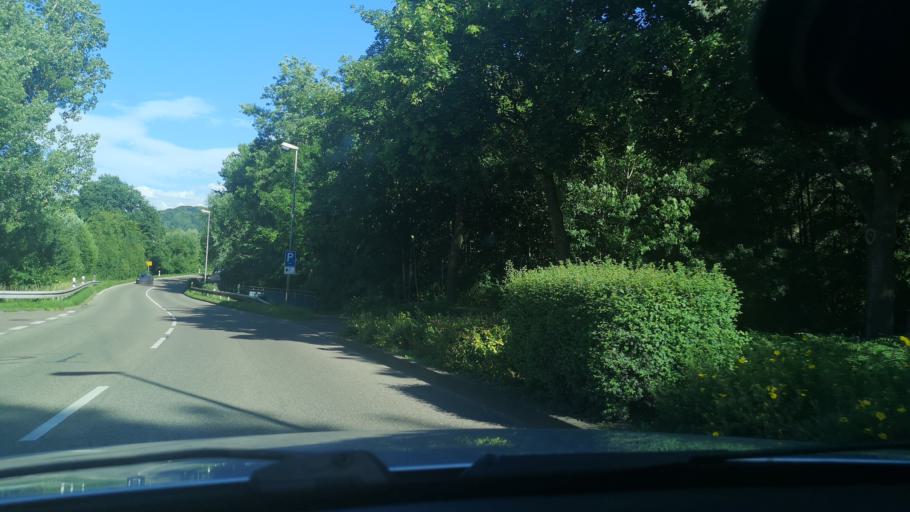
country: DE
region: Baden-Wuerttemberg
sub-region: Regierungsbezirk Stuttgart
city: Heiningen
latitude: 48.6576
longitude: 9.6528
